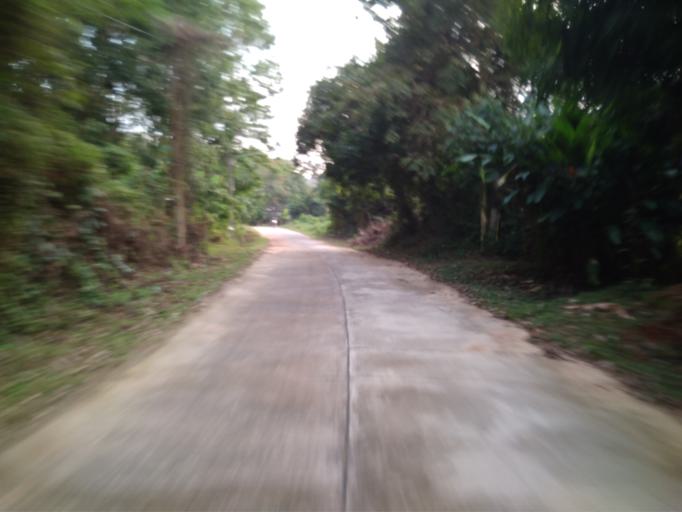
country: TH
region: Phangnga
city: Ko Yao
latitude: 8.1616
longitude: 98.6100
